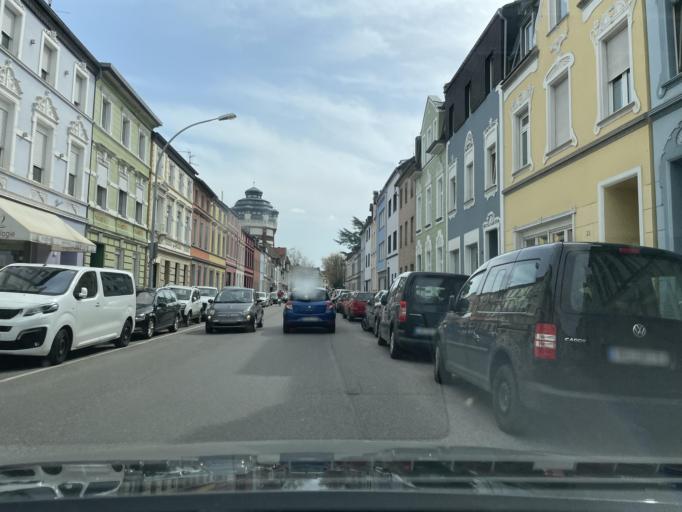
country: DE
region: North Rhine-Westphalia
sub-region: Regierungsbezirk Dusseldorf
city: Monchengladbach
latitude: 51.2016
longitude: 6.4232
